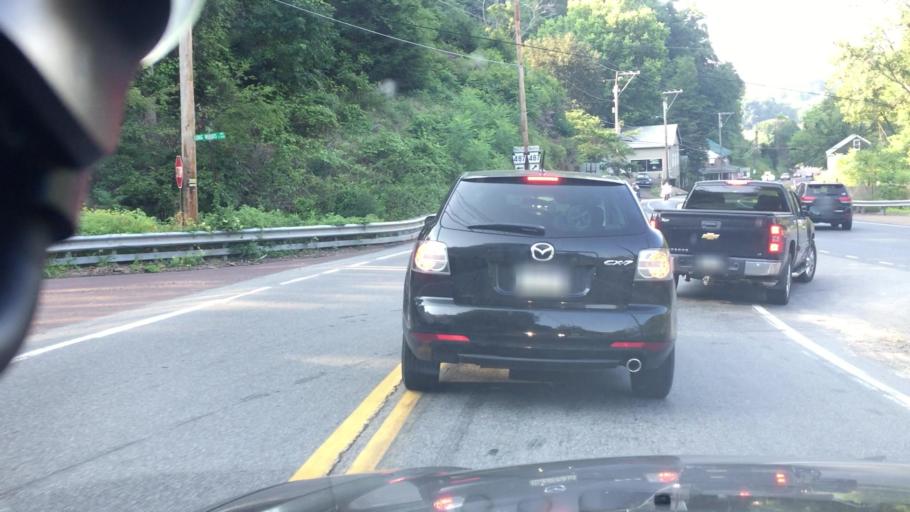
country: US
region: Pennsylvania
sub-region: Columbia County
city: Catawissa
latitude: 40.9422
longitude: -76.4573
